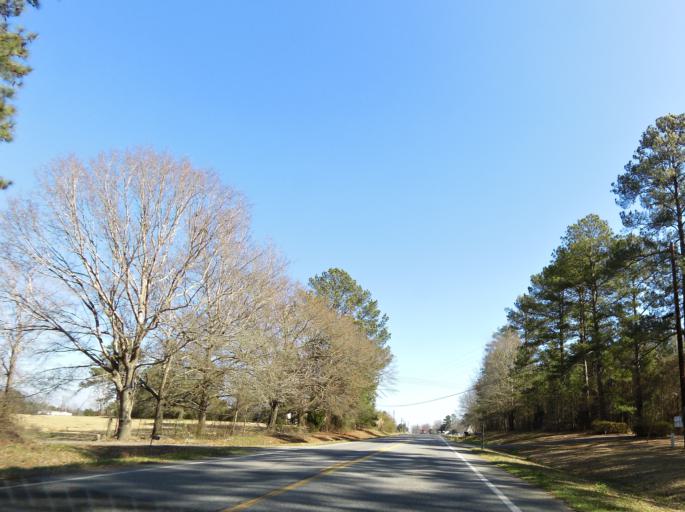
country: US
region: Georgia
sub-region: Bleckley County
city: Cochran
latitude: 32.3716
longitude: -83.3718
